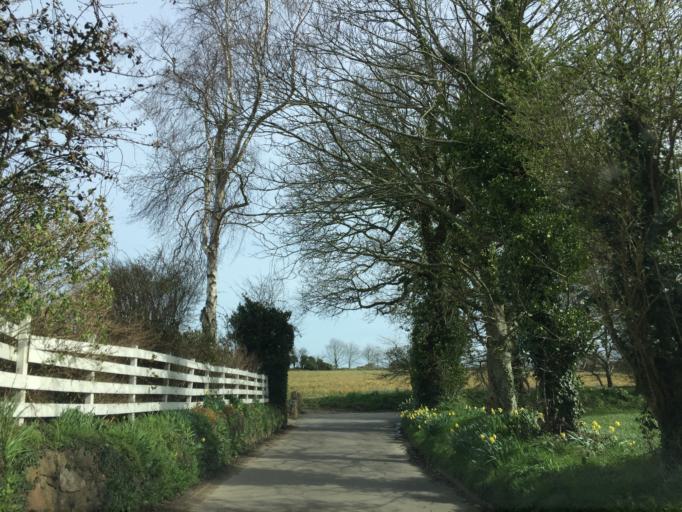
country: JE
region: St Helier
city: Saint Helier
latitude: 49.2276
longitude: -2.1183
